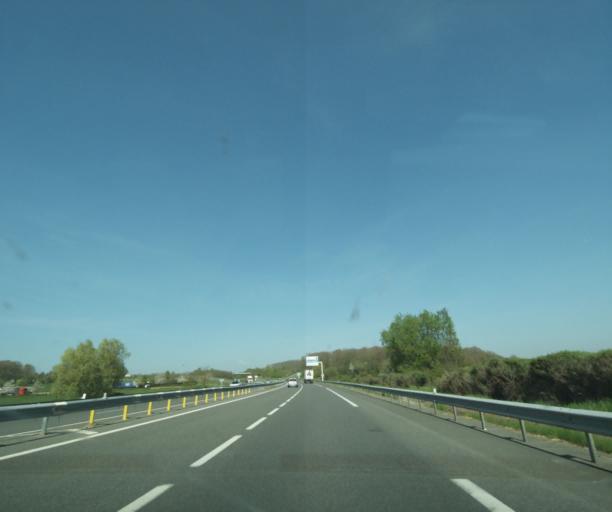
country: FR
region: Bourgogne
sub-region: Departement de la Nievre
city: Pouilly-sur-Loire
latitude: 47.3359
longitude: 2.9307
